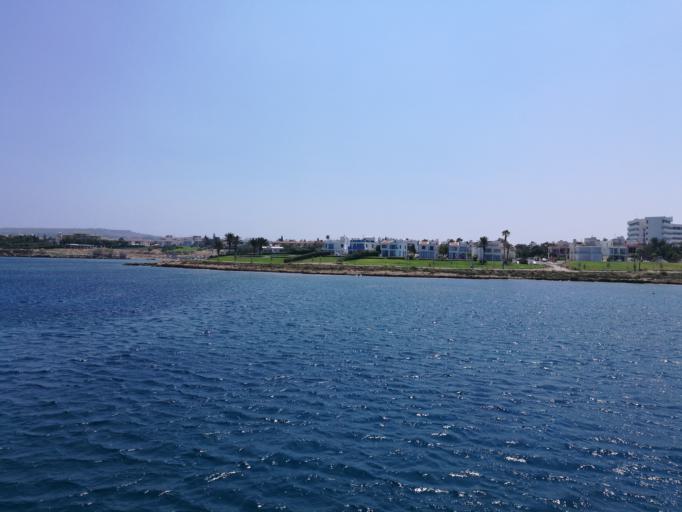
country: CY
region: Ammochostos
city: Protaras
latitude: 35.0447
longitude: 34.0353
